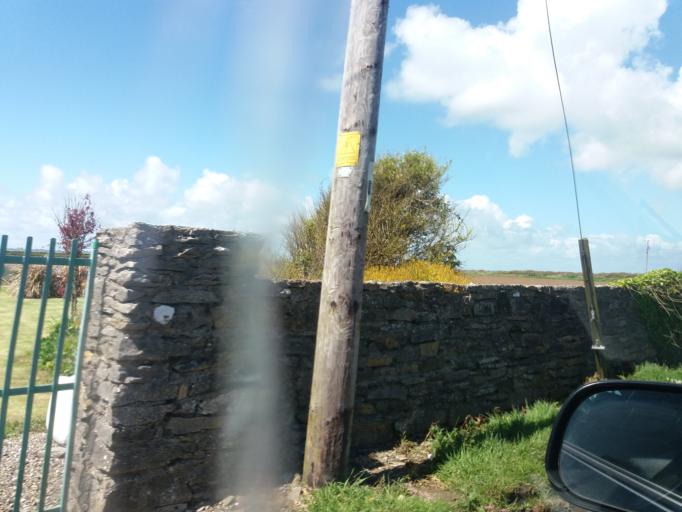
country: IE
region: Munster
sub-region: Waterford
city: Dunmore East
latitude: 52.1361
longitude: -6.9167
